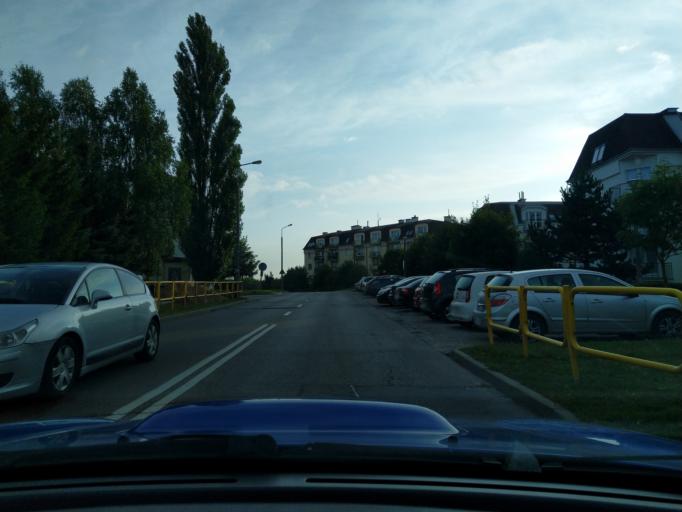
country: PL
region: Warmian-Masurian Voivodeship
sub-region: Olsztyn
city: Kortowo
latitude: 53.7589
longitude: 20.4706
